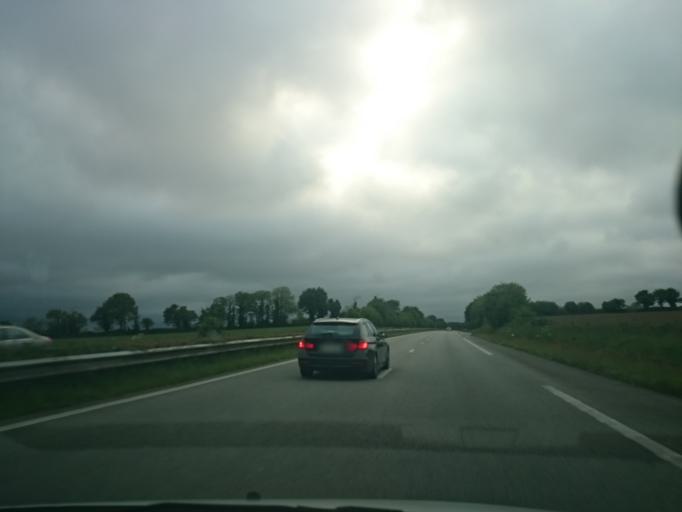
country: FR
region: Brittany
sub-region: Departement du Finistere
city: Saint-Yvi
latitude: 47.9465
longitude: -3.9360
